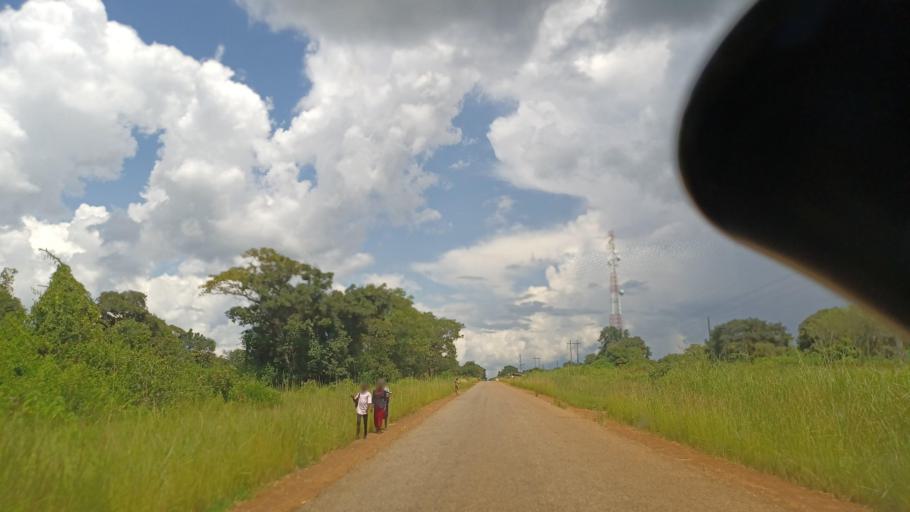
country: ZM
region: North-Western
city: Kasempa
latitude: -12.7832
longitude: 26.0100
